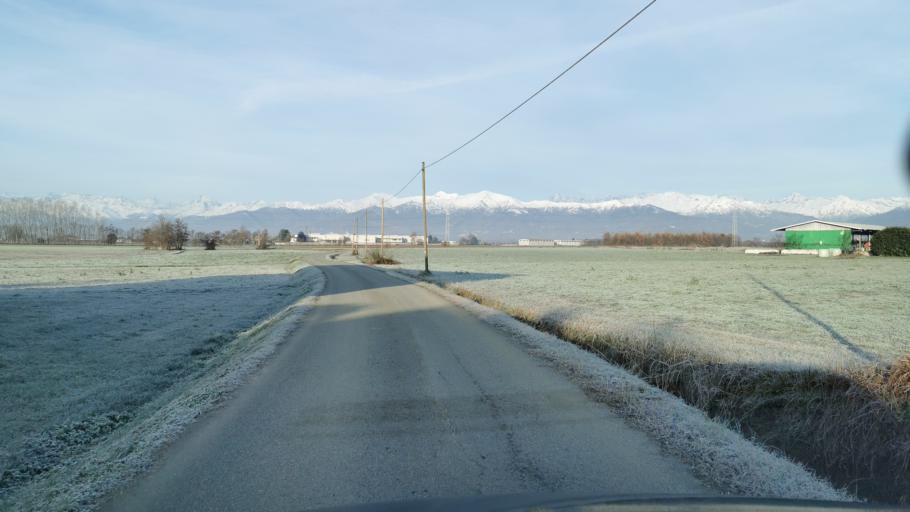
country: IT
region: Piedmont
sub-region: Provincia di Torino
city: Bosconero
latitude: 45.2862
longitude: 7.7610
